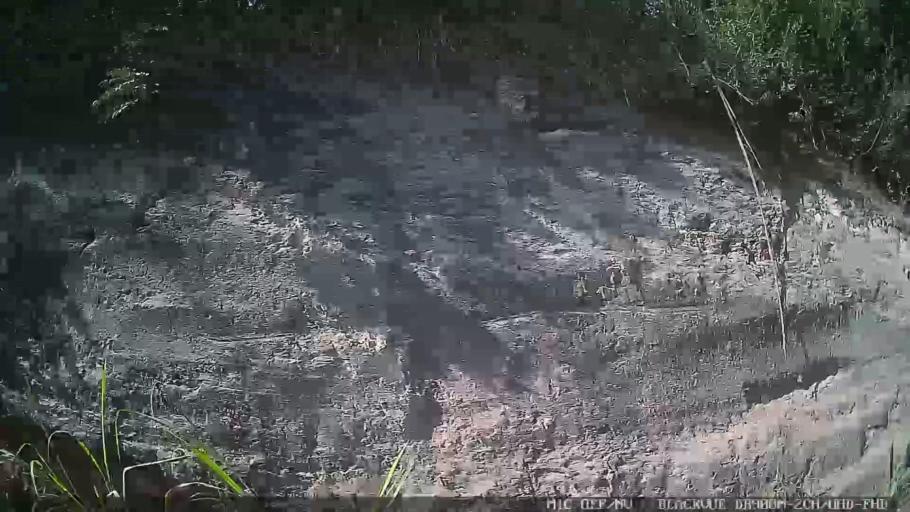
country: BR
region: Sao Paulo
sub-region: Jarinu
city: Jarinu
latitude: -23.0658
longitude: -46.6800
